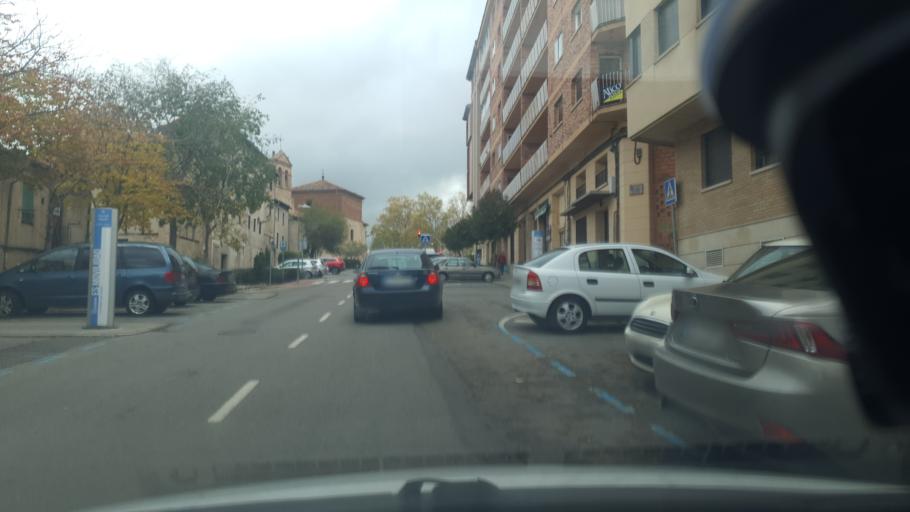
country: ES
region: Castille and Leon
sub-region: Provincia de Segovia
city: Segovia
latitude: 40.9437
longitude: -4.1118
